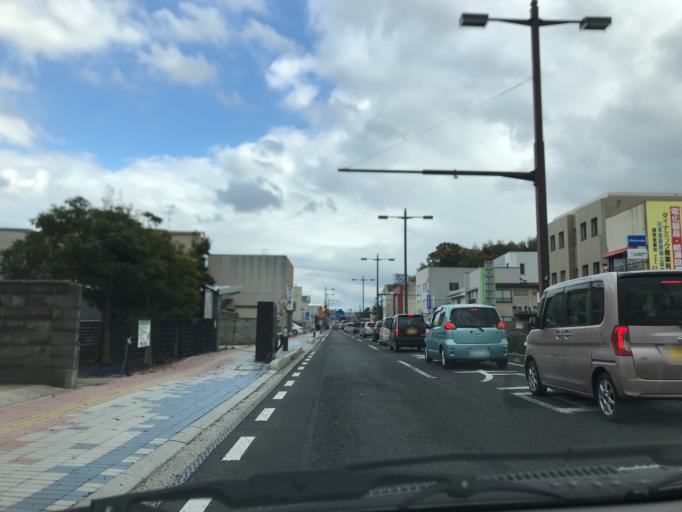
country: JP
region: Shimane
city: Matsue-shi
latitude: 35.4590
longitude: 133.0631
